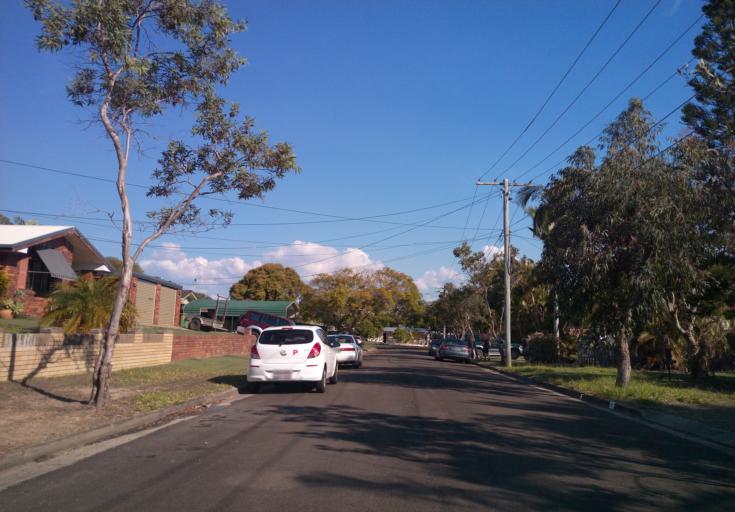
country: AU
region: Queensland
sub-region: Redland
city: Wellington Point
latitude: -27.5110
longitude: 153.2100
